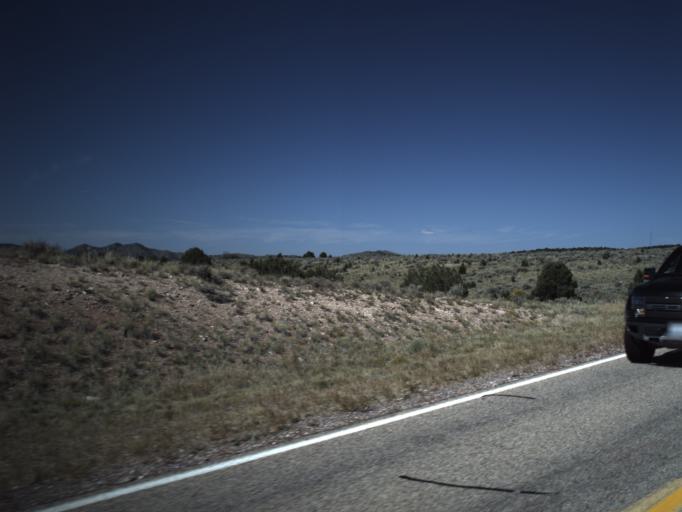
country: US
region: Utah
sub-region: Washington County
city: Enterprise
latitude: 37.6524
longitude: -113.4516
